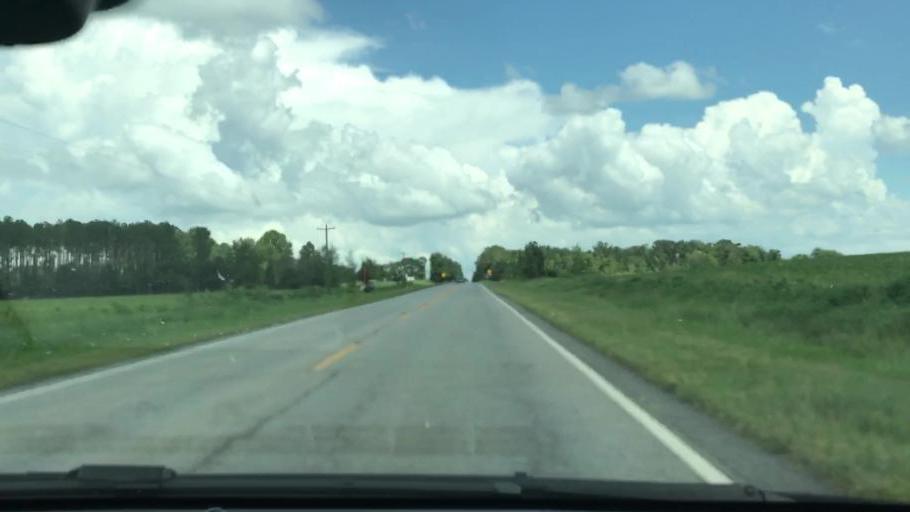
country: US
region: Georgia
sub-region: Seminole County
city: Donalsonville
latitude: 30.9807
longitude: -84.9851
